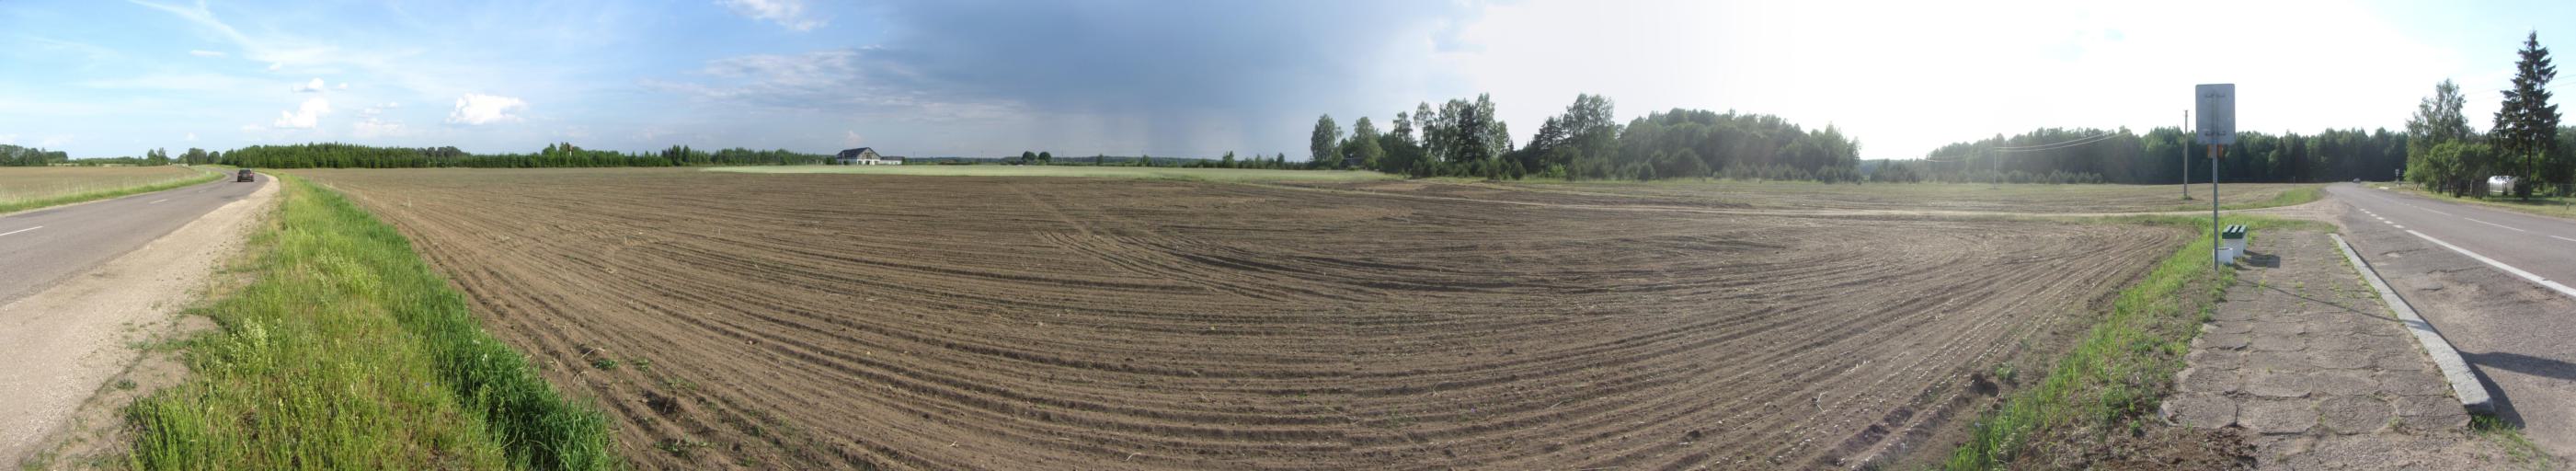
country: LT
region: Kauno apskritis
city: Jonava
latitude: 55.0994
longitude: 24.4553
